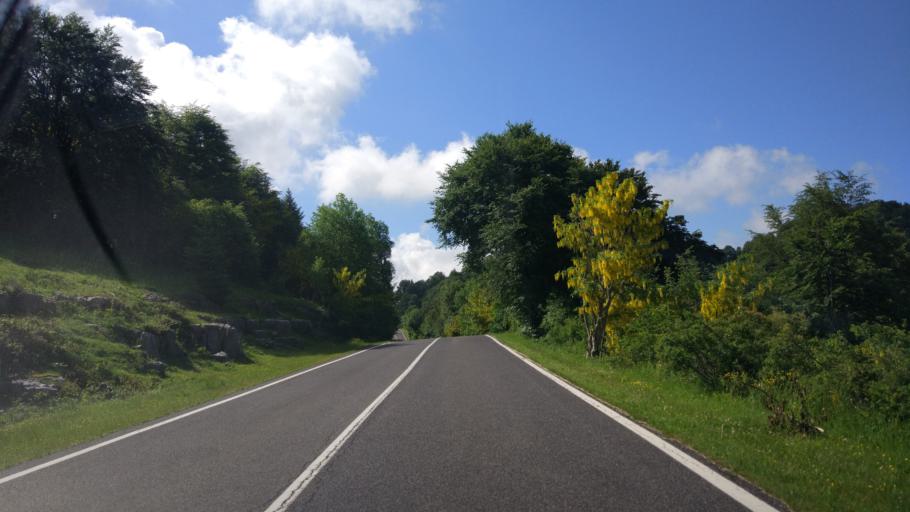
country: IT
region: Veneto
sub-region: Provincia di Verona
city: Velo Veronese
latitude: 45.6609
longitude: 11.0852
